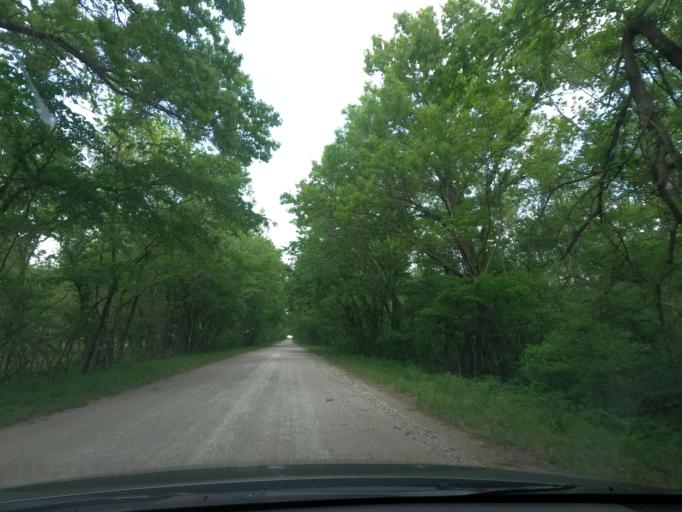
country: US
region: Kansas
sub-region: Labette County
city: Oswego
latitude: 37.3046
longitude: -95.0134
